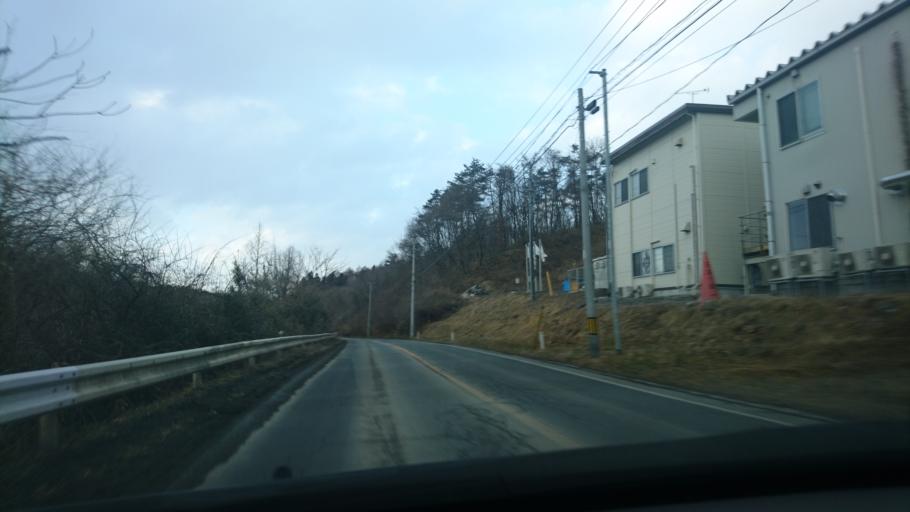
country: JP
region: Iwate
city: Ichinoseki
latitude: 38.9681
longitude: 141.3320
